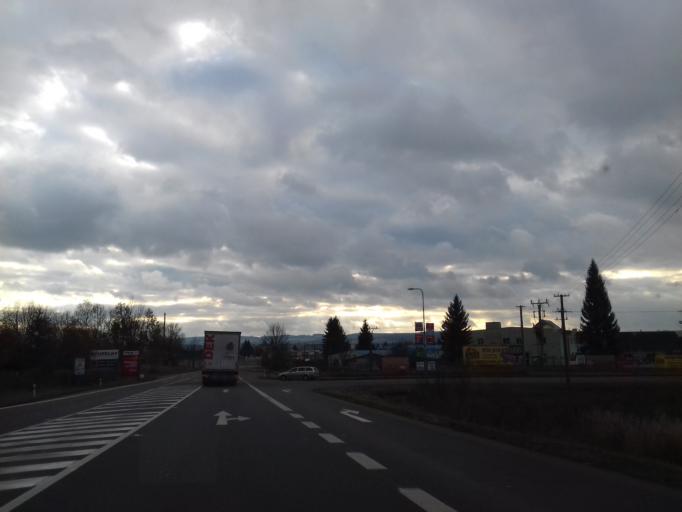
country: CZ
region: Pardubicky
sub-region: Okres Svitavy
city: Svitavy
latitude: 49.7565
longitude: 16.4852
